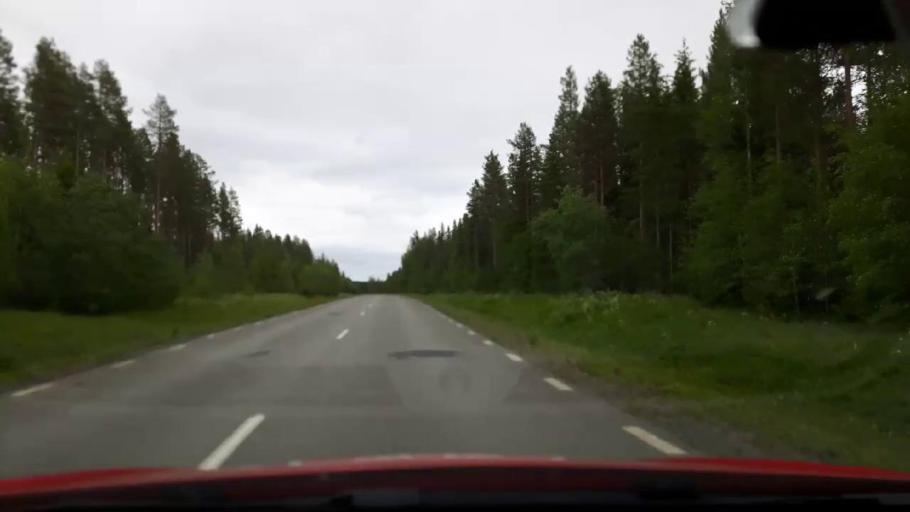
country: SE
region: Jaemtland
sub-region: OEstersunds Kommun
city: Lit
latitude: 63.7326
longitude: 14.9027
